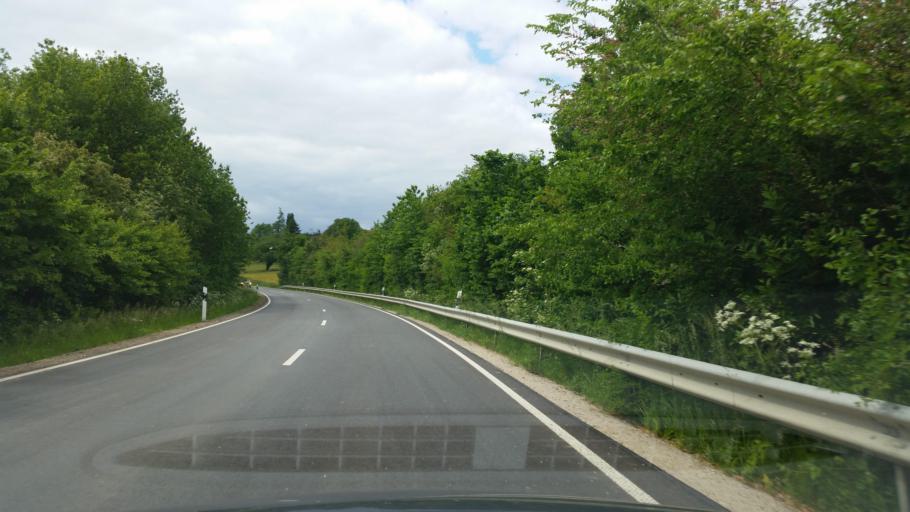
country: DE
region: Schleswig-Holstein
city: Ahrensbok
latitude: 54.0668
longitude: 10.5831
